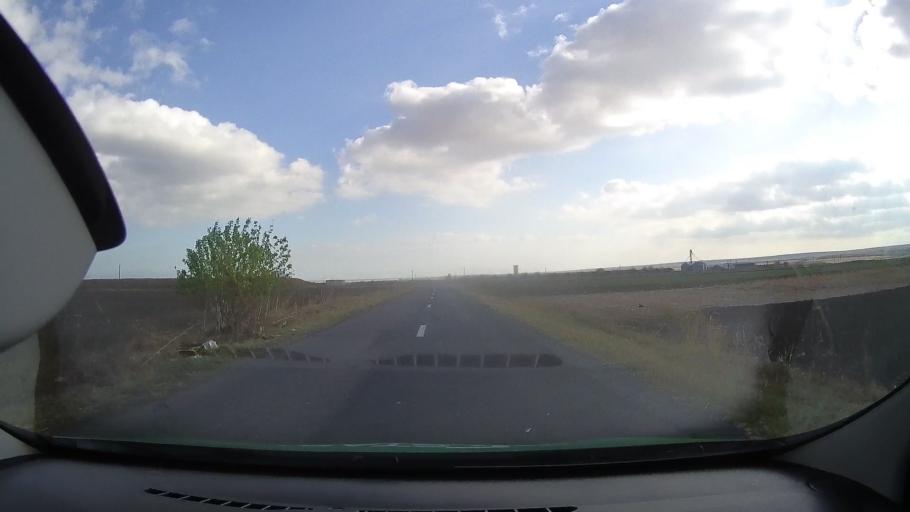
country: RO
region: Constanta
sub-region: Comuna Cogealac
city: Tariverde
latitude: 44.5519
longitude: 28.6252
